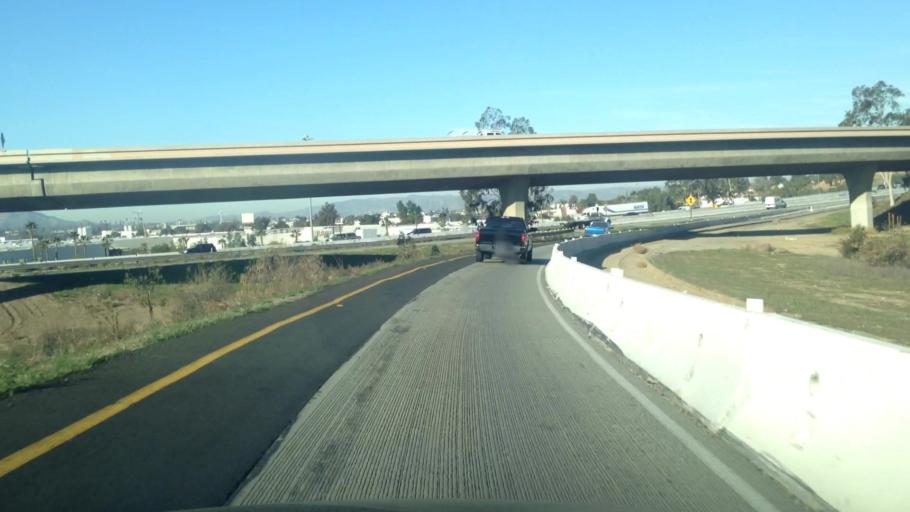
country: US
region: California
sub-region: Riverside County
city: Corona
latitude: 33.8832
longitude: -117.5466
